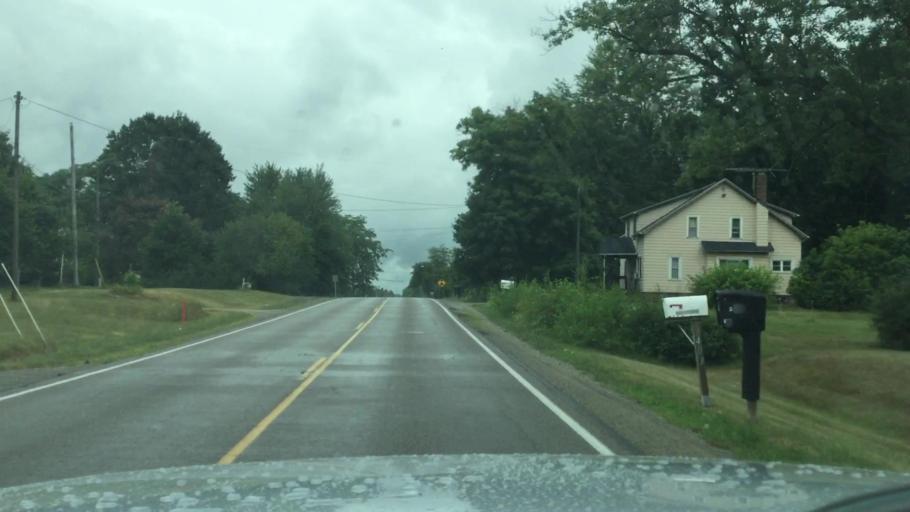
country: US
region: Michigan
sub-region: Genesee County
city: Beecher
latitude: 43.0754
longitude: -83.7489
